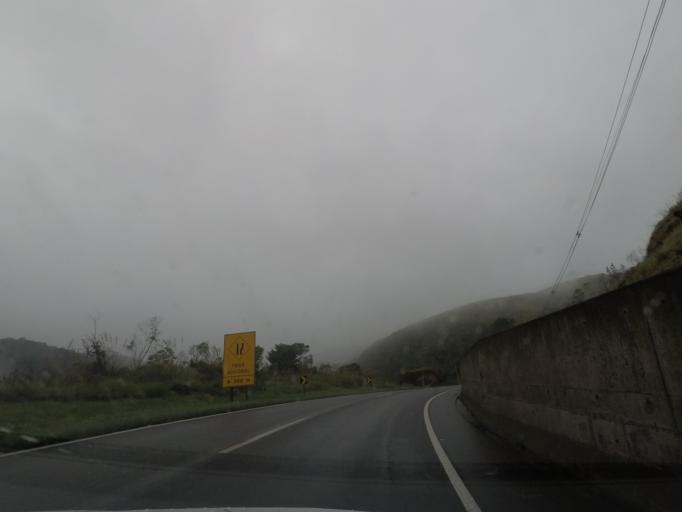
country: BR
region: Sao Paulo
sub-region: Cajati
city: Cajati
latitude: -24.9654
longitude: -48.4631
